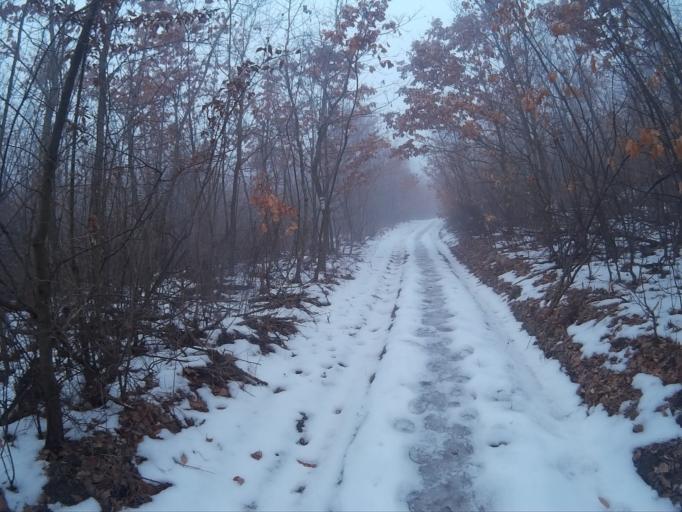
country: HU
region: Nograd
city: Matraverebely
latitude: 47.9880
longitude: 19.7624
